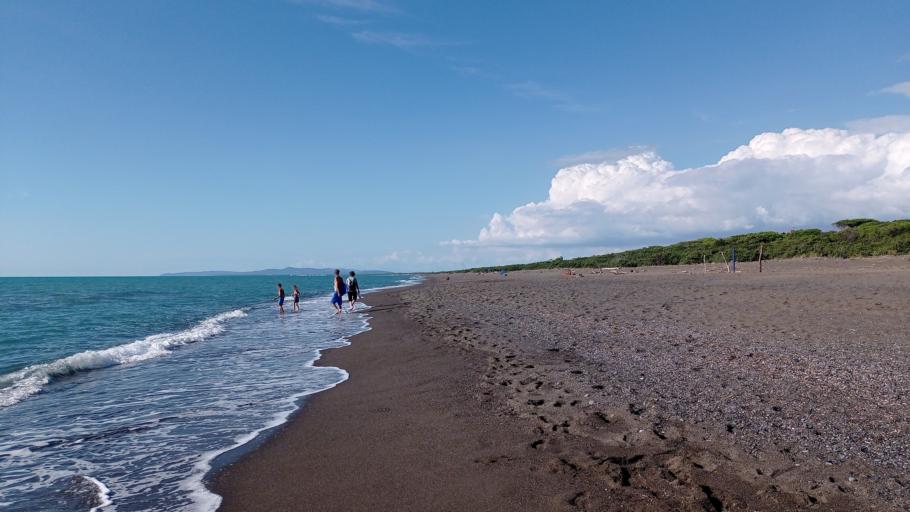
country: IT
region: Tuscany
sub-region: Provincia di Livorno
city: Donoratico
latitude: 43.1966
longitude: 10.5351
